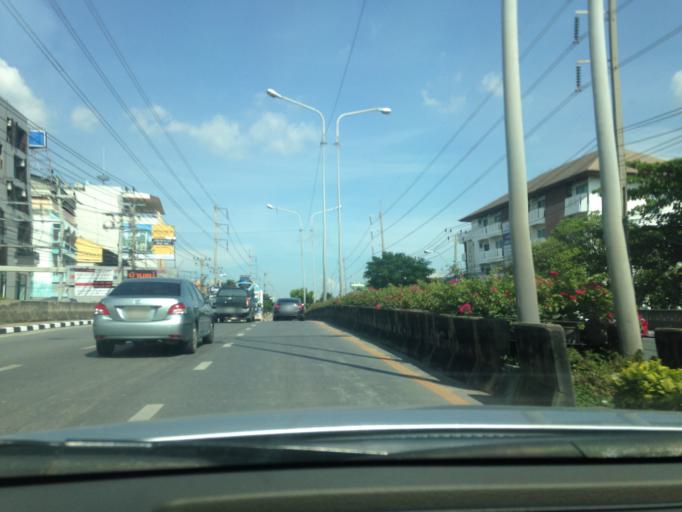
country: TH
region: Bangkok
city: Lat Krabang
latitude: 13.7223
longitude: 100.7290
